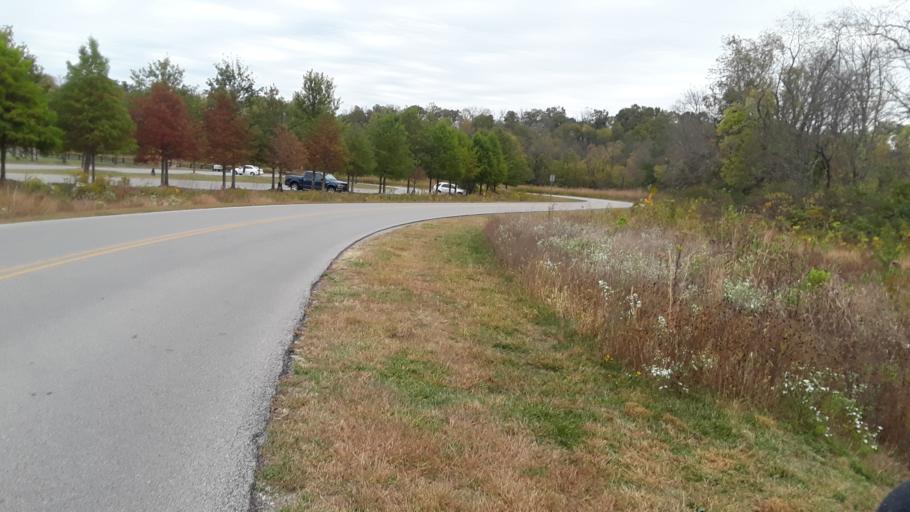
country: US
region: Kentucky
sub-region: Jefferson County
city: Middletown
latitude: 38.2086
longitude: -85.4743
